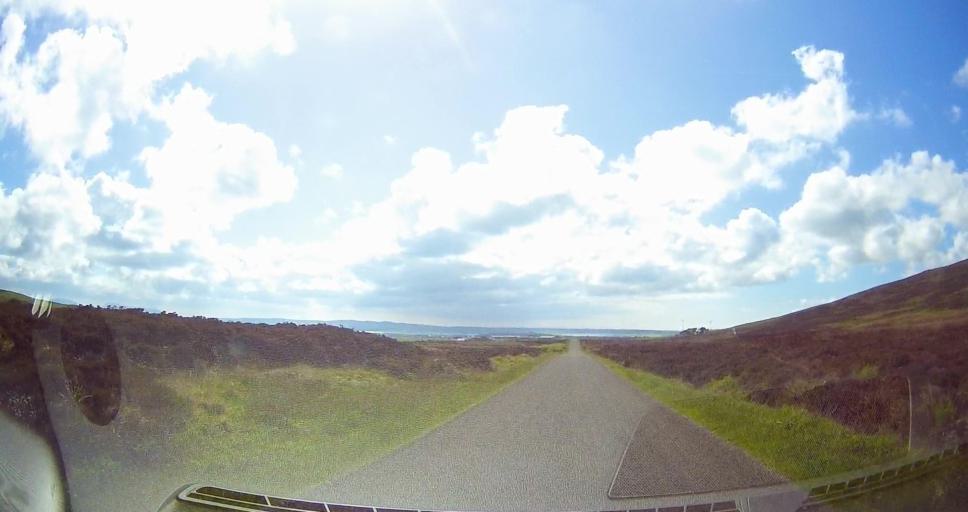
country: GB
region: Scotland
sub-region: Orkney Islands
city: Stromness
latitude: 59.0471
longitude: -3.1339
